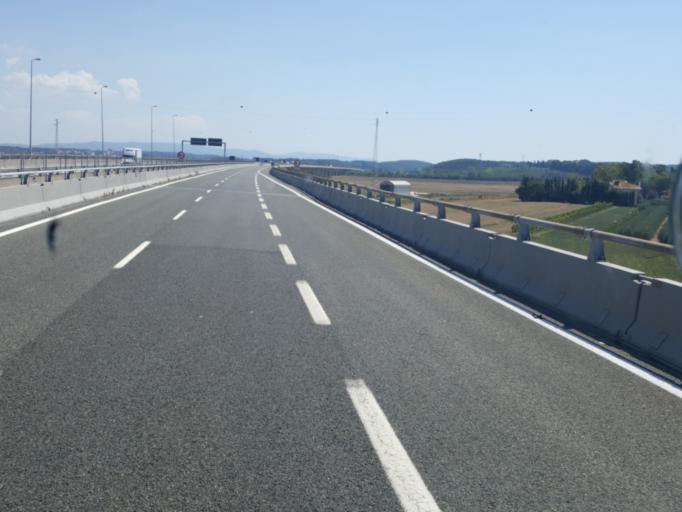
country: IT
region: Tuscany
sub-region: Provincia di Livorno
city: Vicarello
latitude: 43.6120
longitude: 10.4411
